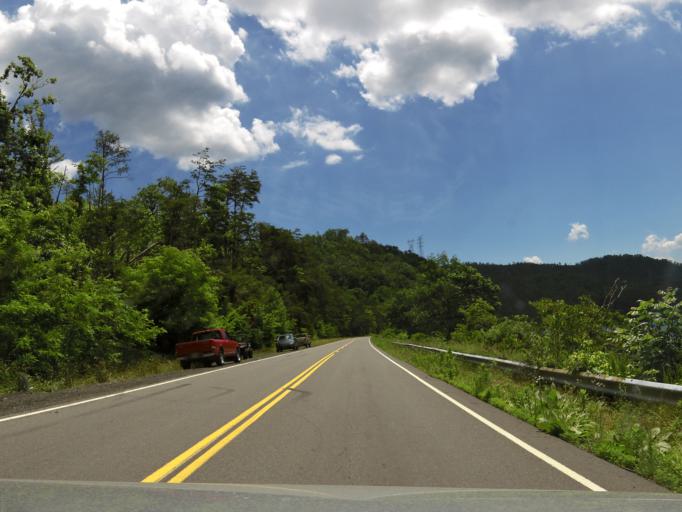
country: US
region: Tennessee
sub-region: Blount County
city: Maryville
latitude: 35.5553
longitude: -83.9981
